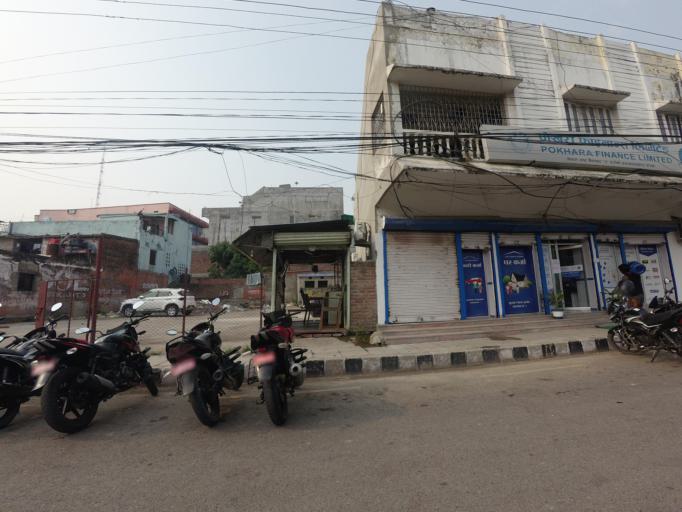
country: NP
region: Western Region
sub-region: Lumbini Zone
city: Bhairahawa
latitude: 27.5090
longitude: 83.4521
